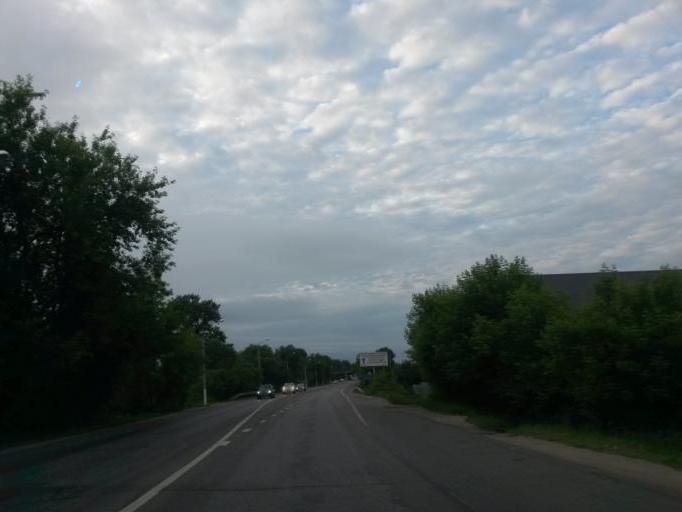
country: RU
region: Moskovskaya
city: Stolbovaya
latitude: 55.2261
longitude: 37.5033
